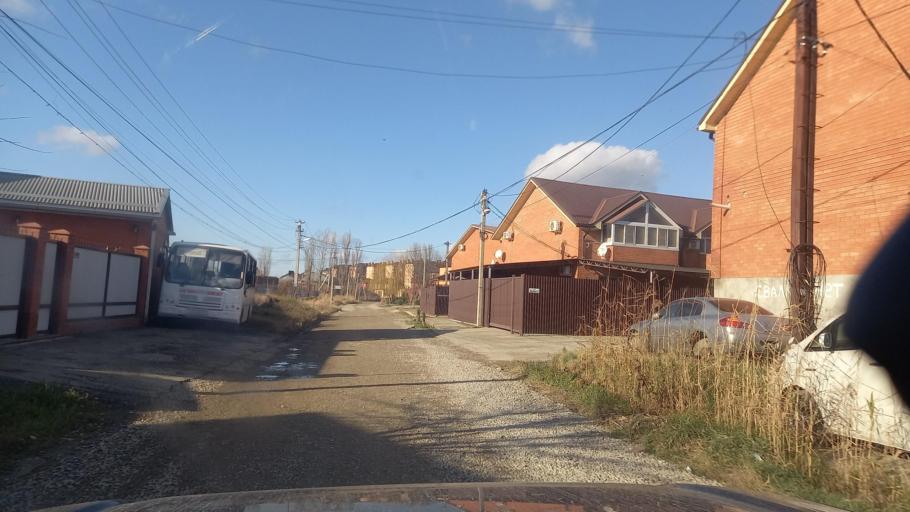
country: RU
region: Adygeya
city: Yablonovskiy
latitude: 44.9938
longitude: 38.9396
